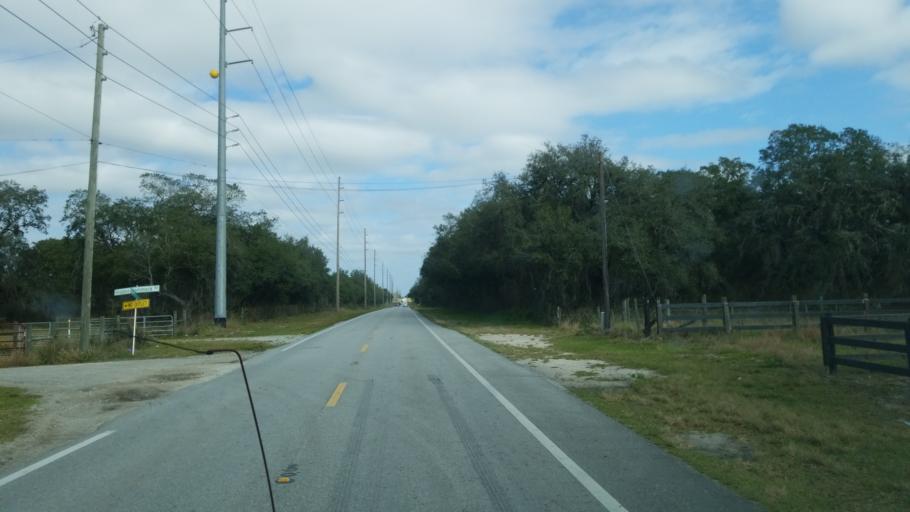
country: US
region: Florida
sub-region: Polk County
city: Lake Wales
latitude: 27.9394
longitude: -81.5377
